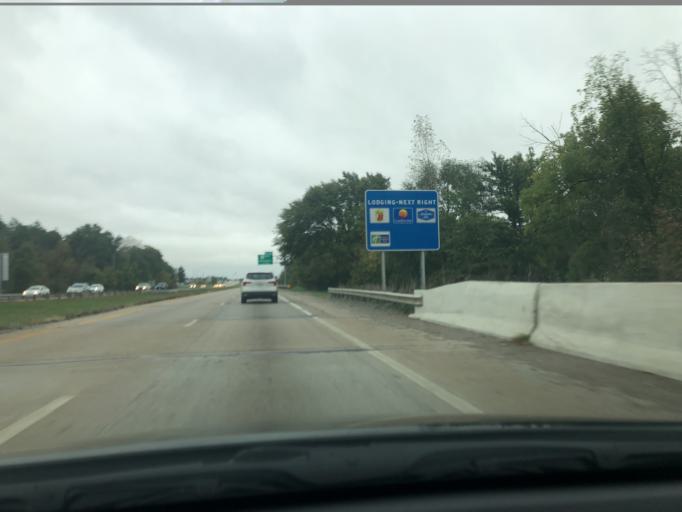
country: US
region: Ohio
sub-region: Union County
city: Marysville
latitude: 40.2453
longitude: -83.3543
